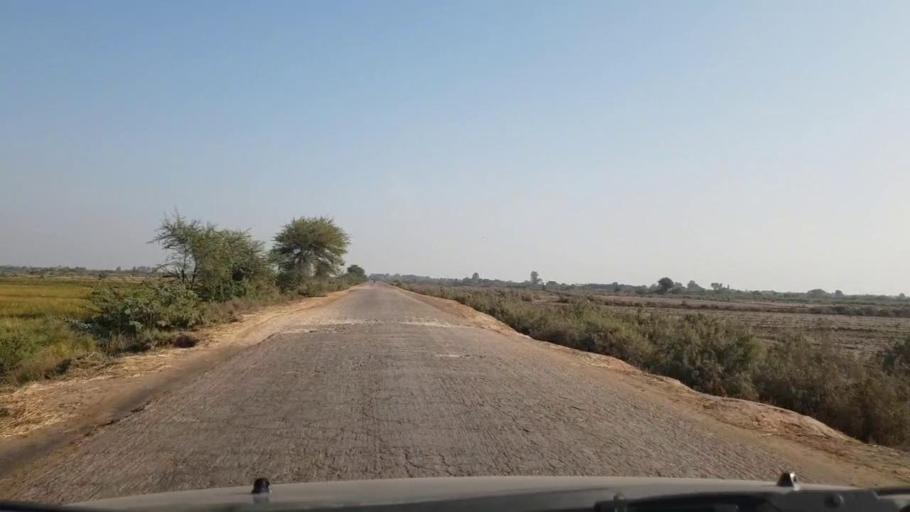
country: PK
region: Sindh
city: Tando Bago
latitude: 24.8643
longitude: 69.0499
